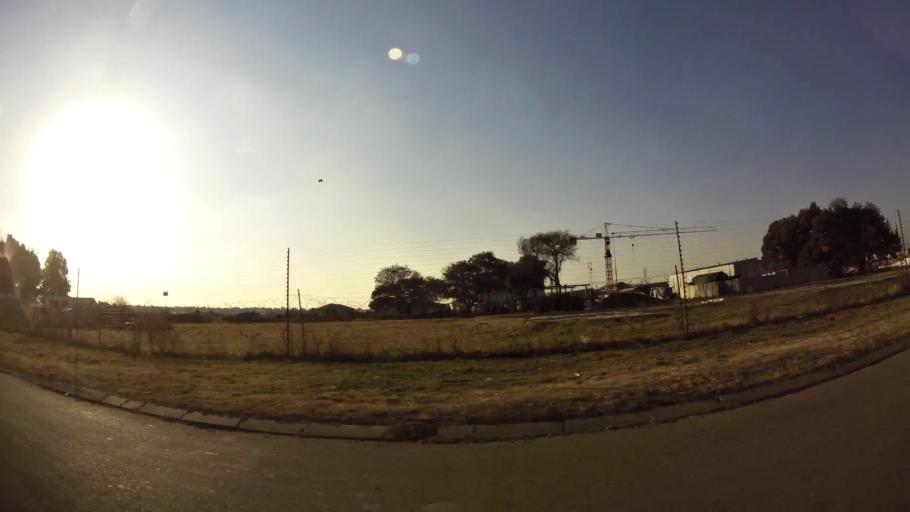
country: ZA
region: Gauteng
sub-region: West Rand District Municipality
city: Randfontein
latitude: -26.2025
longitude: 27.6869
